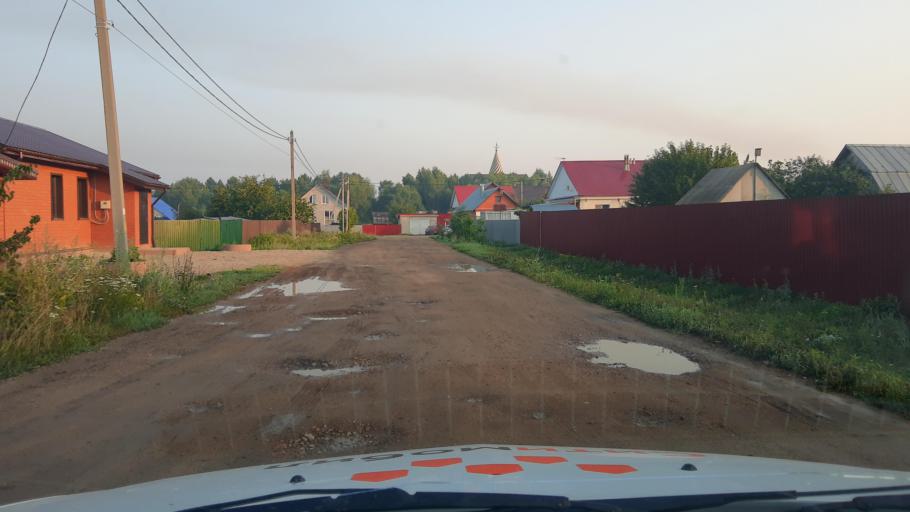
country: RU
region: Bashkortostan
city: Iglino
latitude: 54.7432
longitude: 56.2773
